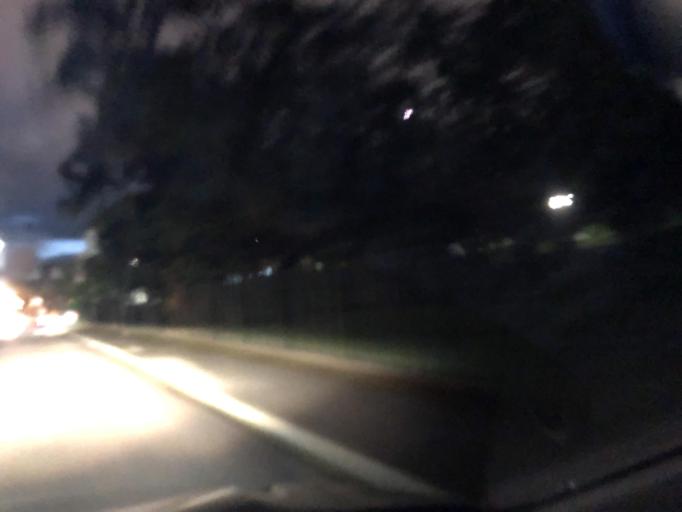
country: BR
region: Santa Catarina
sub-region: Florianopolis
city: Carvoeira
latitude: -27.6017
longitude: -48.5255
